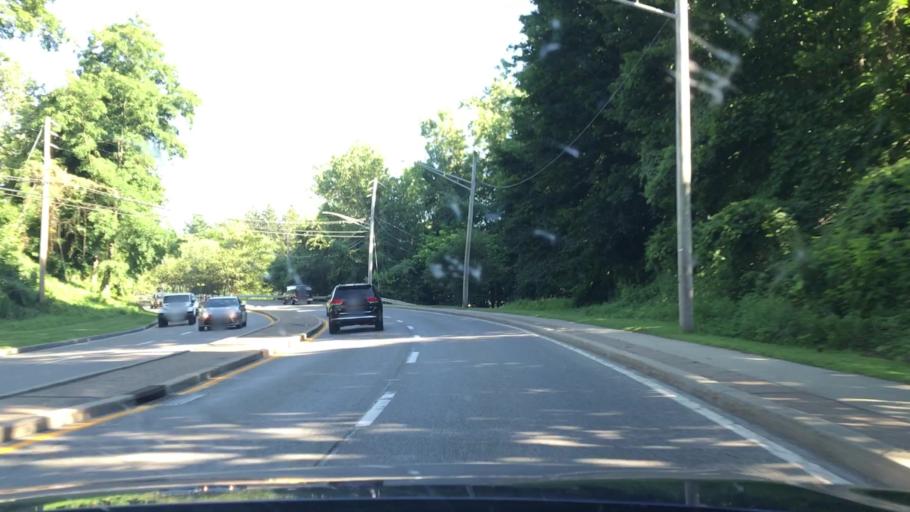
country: US
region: New York
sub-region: Westchester County
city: Thornwood
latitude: 41.1199
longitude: -73.7752
